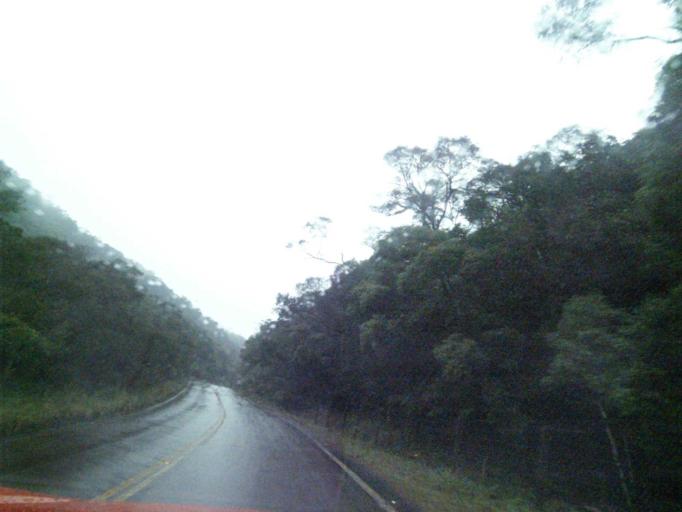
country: BR
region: Santa Catarina
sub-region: Anitapolis
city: Anitapolis
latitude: -27.7715
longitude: -49.0408
